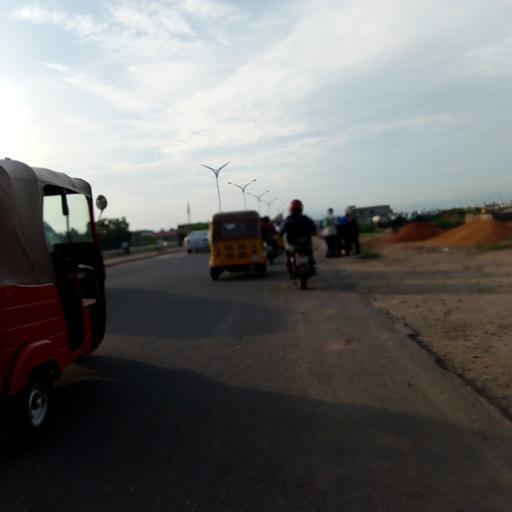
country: TG
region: Maritime
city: Lome
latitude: 6.1903
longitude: 1.2737
